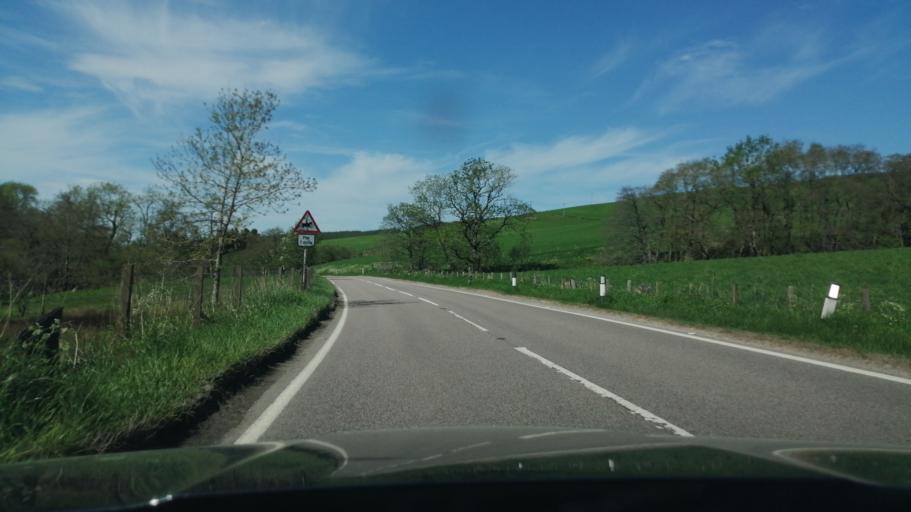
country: GB
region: Scotland
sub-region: Moray
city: Dufftown
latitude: 57.5058
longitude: -3.1240
